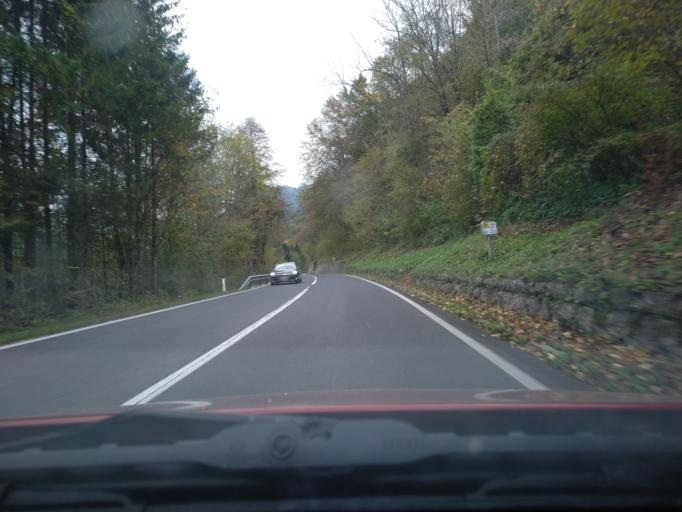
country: IT
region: Friuli Venezia Giulia
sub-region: Provincia di Udine
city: Cras
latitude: 46.2132
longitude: 13.6177
